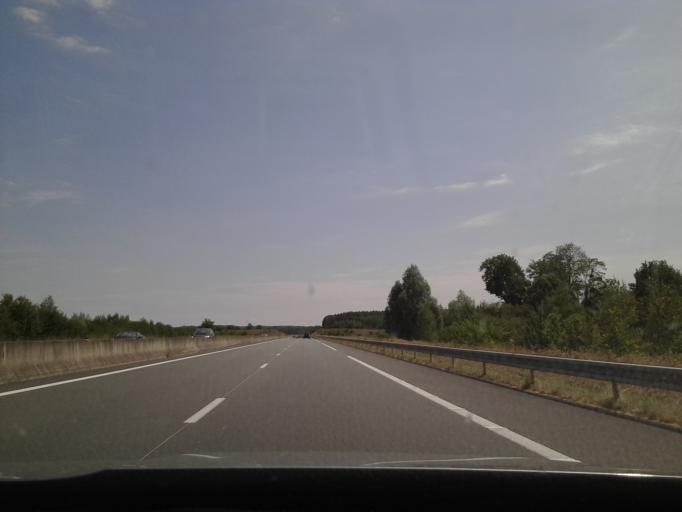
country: FR
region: Pays de la Loire
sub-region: Departement de la Sarthe
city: Chateau-du-Loir
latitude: 47.6606
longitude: 0.4081
